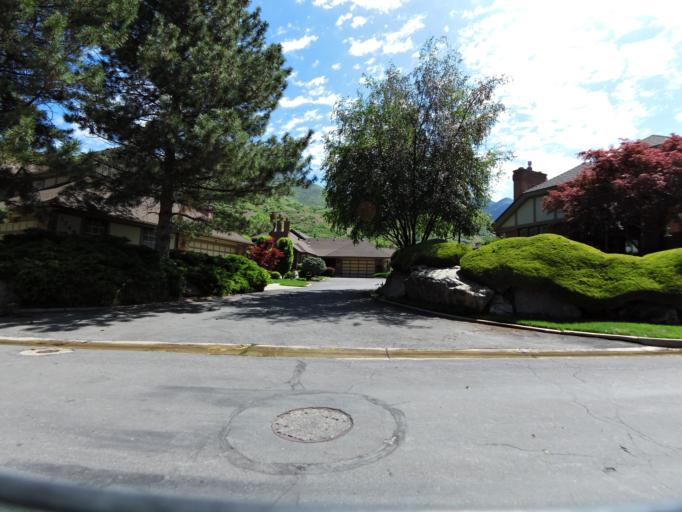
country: US
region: Utah
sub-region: Weber County
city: Uintah
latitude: 41.1777
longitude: -111.9344
